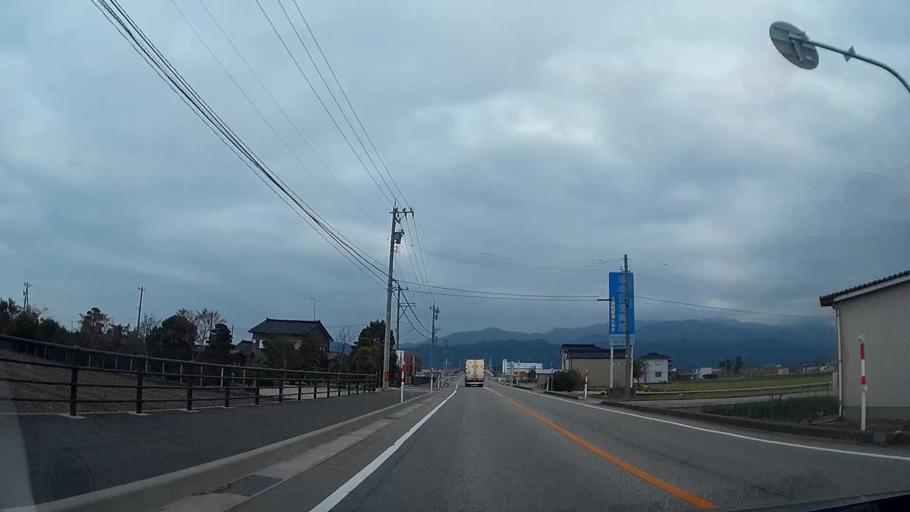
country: JP
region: Toyama
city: Nyuzen
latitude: 36.9455
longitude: 137.5353
